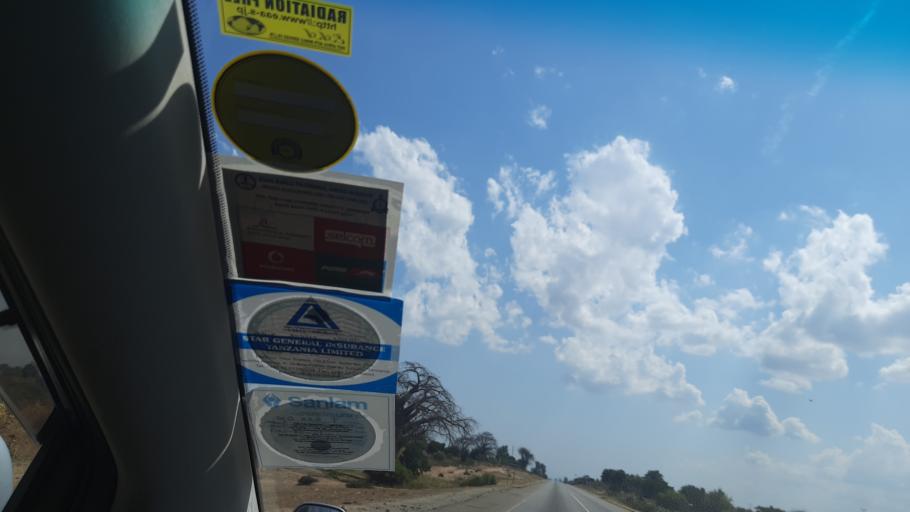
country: TZ
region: Singida
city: Kintinku
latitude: -6.0099
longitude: 35.4192
